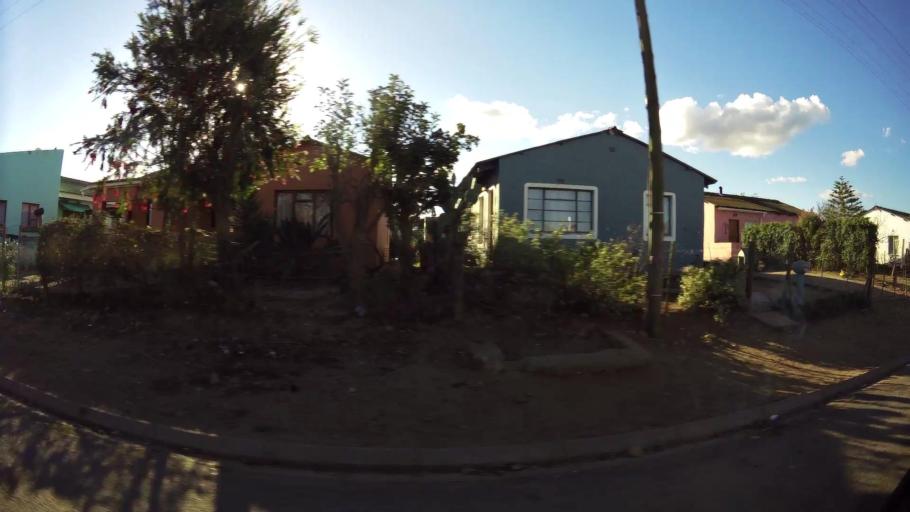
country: ZA
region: Western Cape
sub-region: Eden District Municipality
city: Riversdale
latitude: -34.1030
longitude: 20.9680
